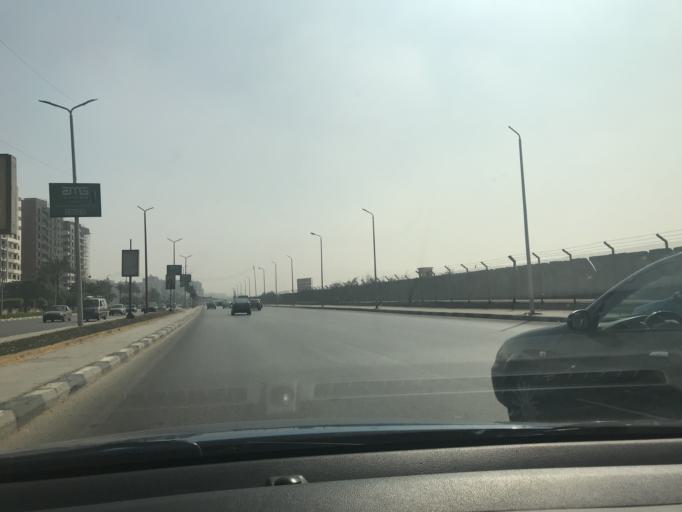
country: EG
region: Muhafazat al Qalyubiyah
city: Al Khankah
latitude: 30.1287
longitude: 31.3821
